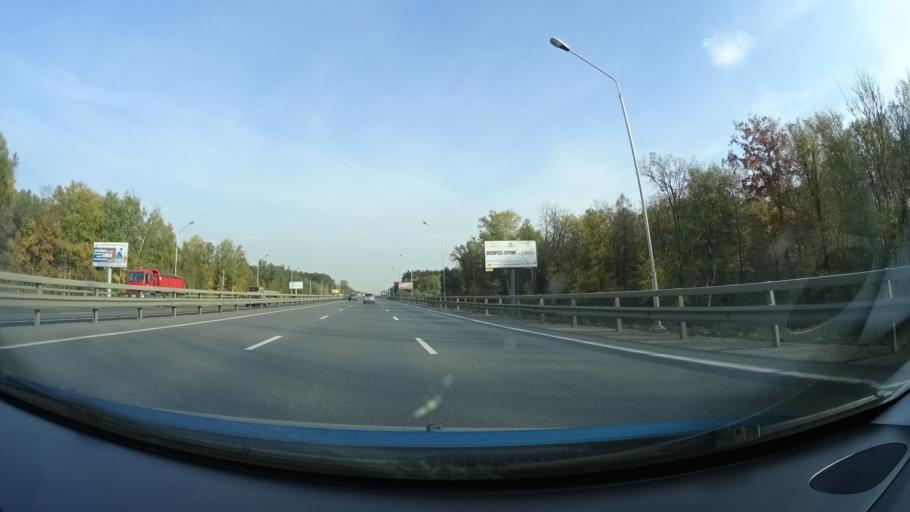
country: RU
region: Bashkortostan
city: Avdon
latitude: 54.6722
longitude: 55.8296
